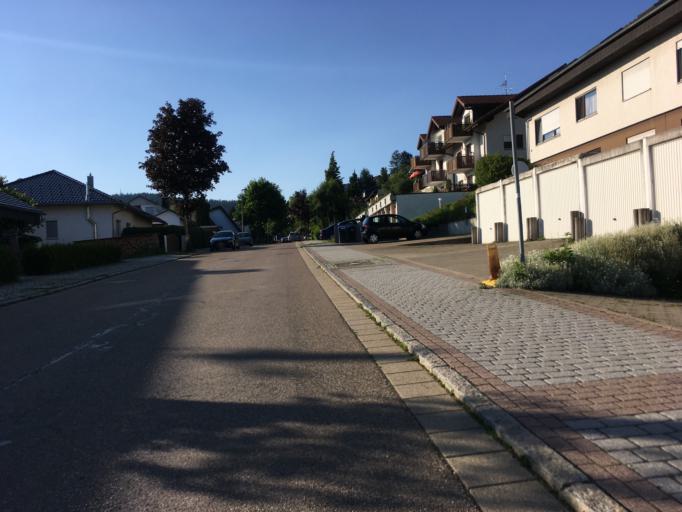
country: DE
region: Baden-Wuerttemberg
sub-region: Freiburg Region
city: Titisee-Neustadt
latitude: 47.9155
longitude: 8.2213
